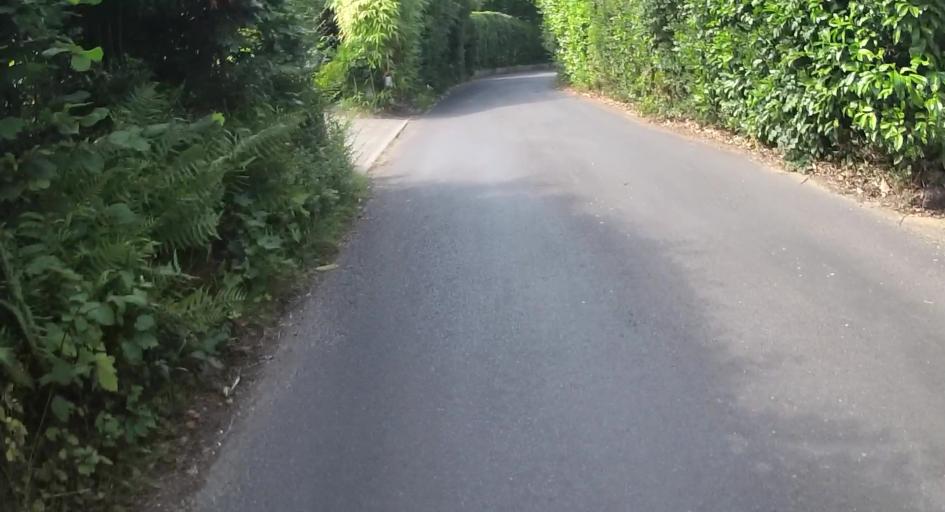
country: GB
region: England
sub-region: Surrey
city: Farnham
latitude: 51.1958
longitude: -0.7995
